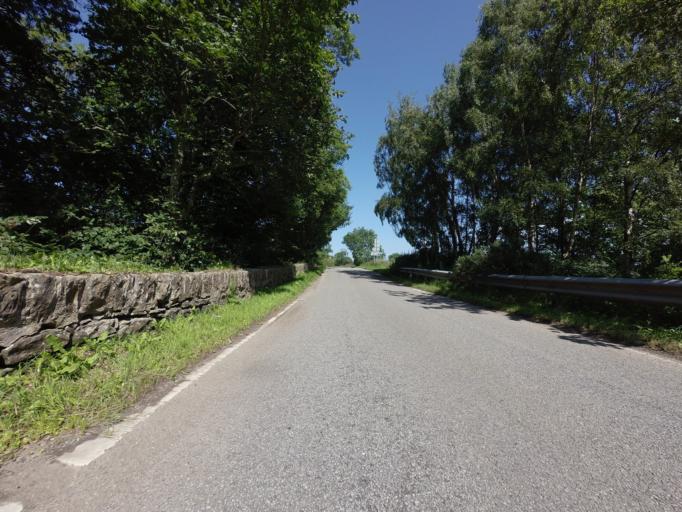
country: GB
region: Scotland
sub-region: Highland
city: Dingwall
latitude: 57.6109
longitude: -4.4174
